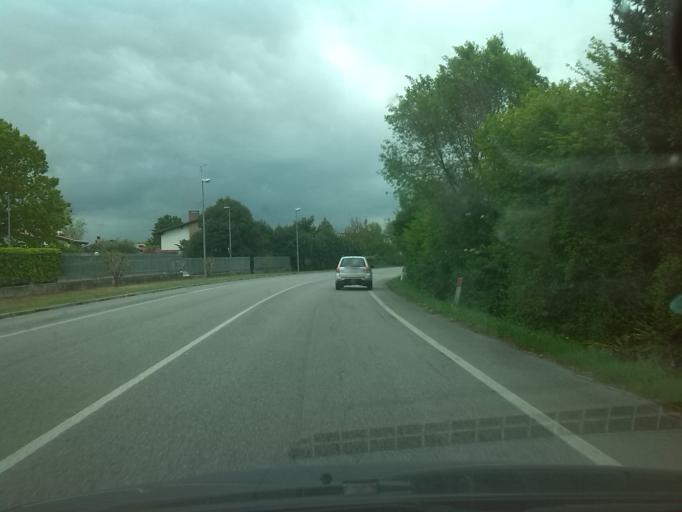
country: IT
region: Friuli Venezia Giulia
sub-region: Provincia di Gorizia
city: Gradisca d'Isonzo
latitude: 45.8941
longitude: 13.5012
